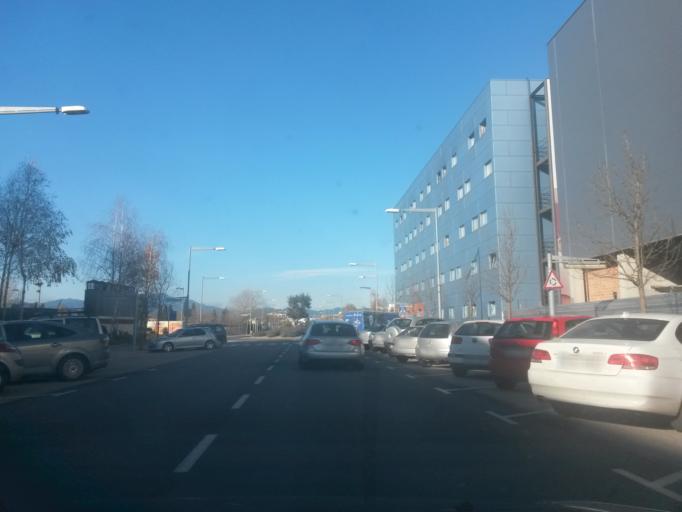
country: ES
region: Catalonia
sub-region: Provincia de Girona
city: Salt
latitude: 41.9671
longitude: 2.7836
